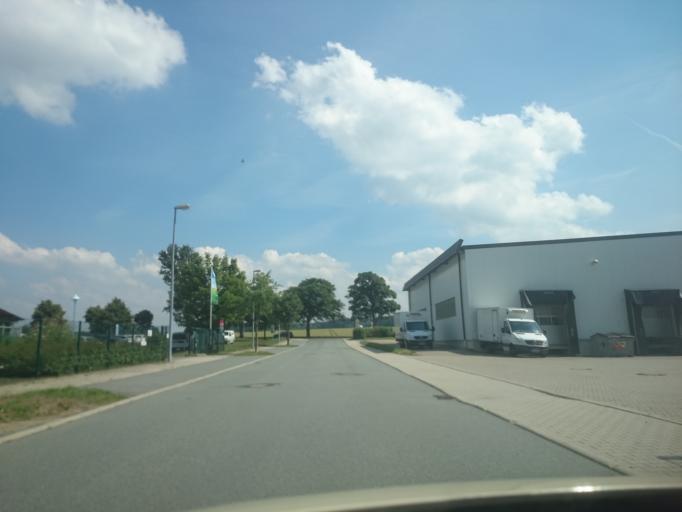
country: DE
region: Saxony
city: Grossruckerswalde
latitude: 50.6746
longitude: 13.1222
